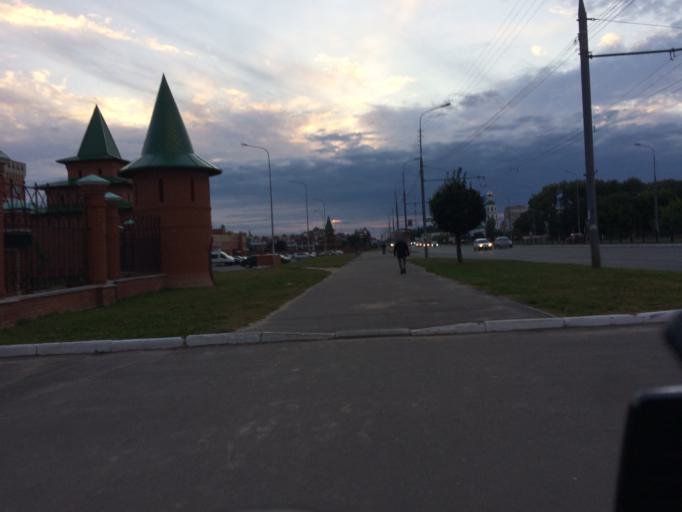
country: RU
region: Mariy-El
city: Yoshkar-Ola
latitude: 56.6375
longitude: 47.9103
